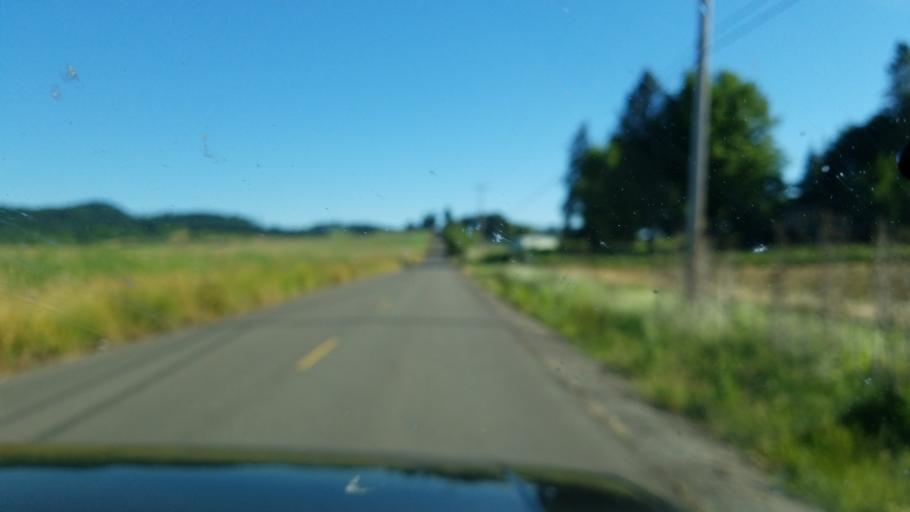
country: US
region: Oregon
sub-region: Yamhill County
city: McMinnville
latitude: 45.2327
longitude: -123.2310
